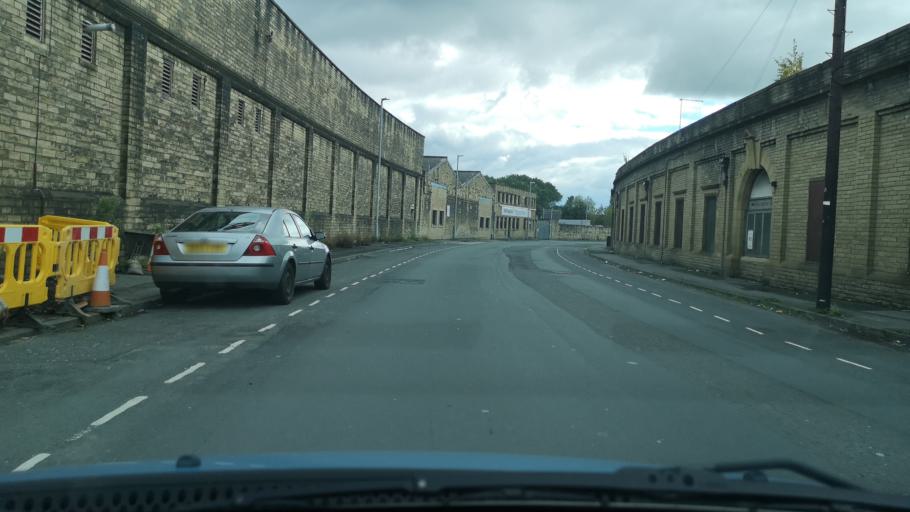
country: GB
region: England
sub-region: Kirklees
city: Dewsbury
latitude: 53.6859
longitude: -1.6243
